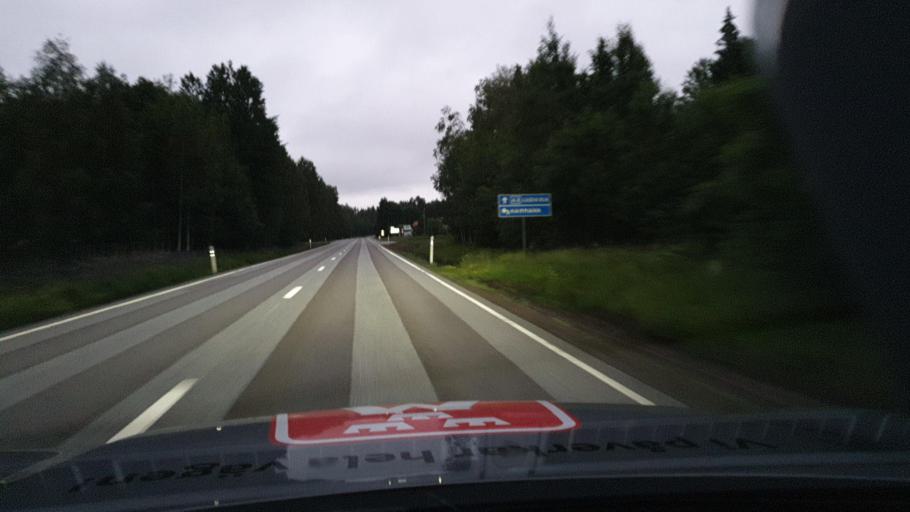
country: SE
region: OErebro
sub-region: Hallefors Kommun
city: Haellefors
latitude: 59.7455
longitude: 14.4958
